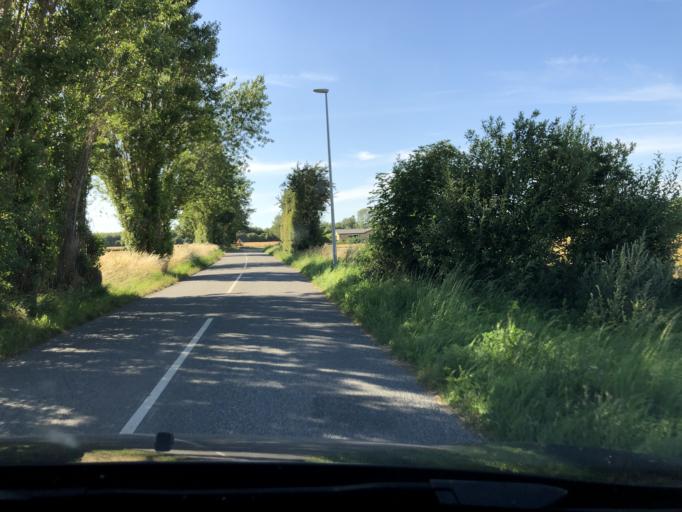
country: DK
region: South Denmark
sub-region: AEro Kommune
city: Marstal
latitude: 54.8635
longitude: 10.5049
